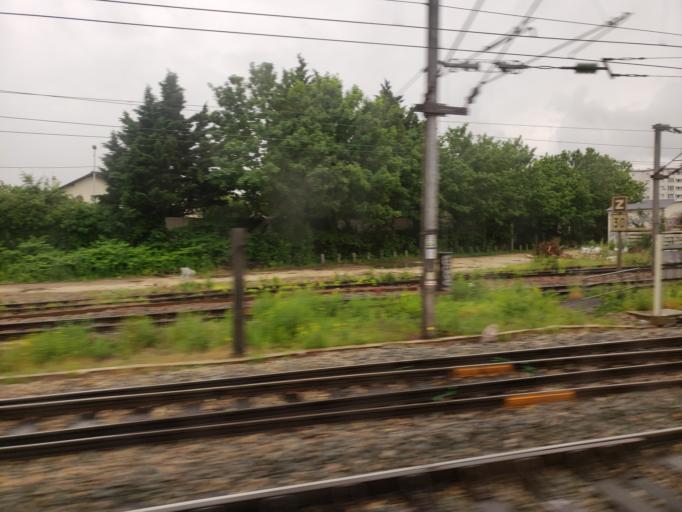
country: FR
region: Ile-de-France
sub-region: Departement de Seine-Saint-Denis
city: Aulnay-sous-Bois
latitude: 48.9321
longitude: 2.4895
